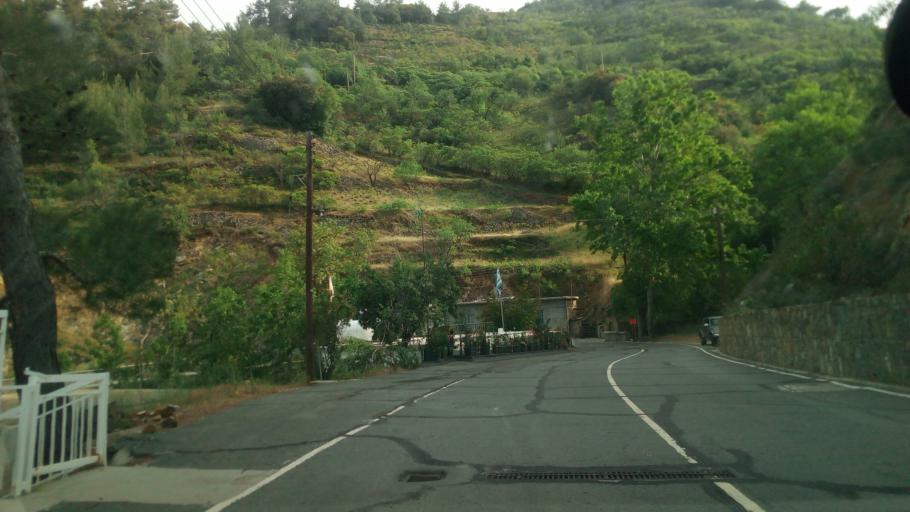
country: CY
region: Lefkosia
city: Kakopetria
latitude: 34.9980
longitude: 32.8054
